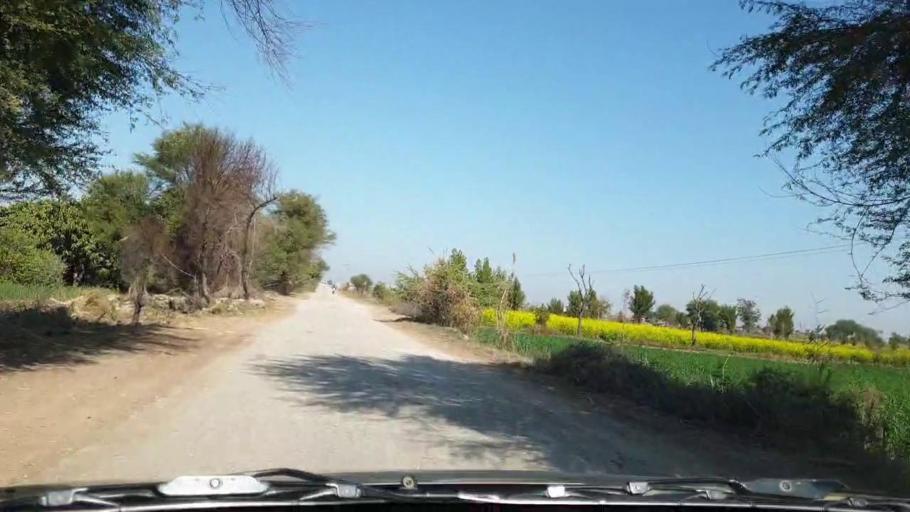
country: PK
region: Sindh
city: Sinjhoro
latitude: 26.1118
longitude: 68.8196
